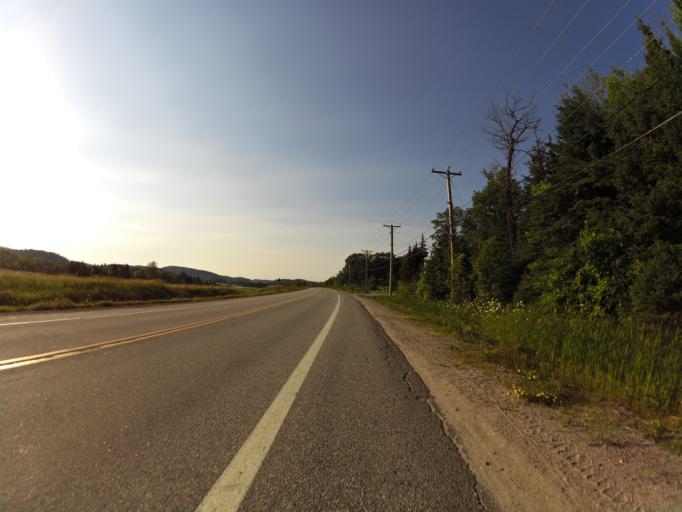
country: CA
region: Quebec
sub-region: Outaouais
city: Wakefield
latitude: 45.5884
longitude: -75.8891
